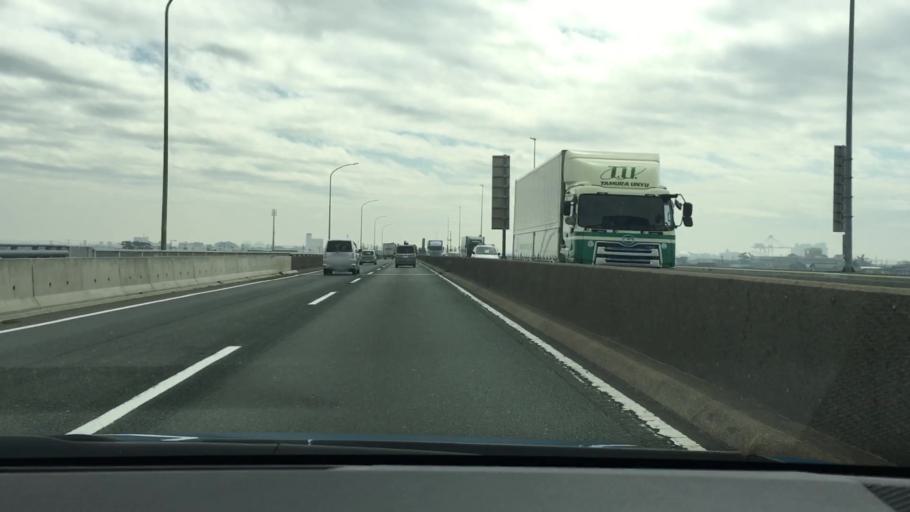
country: JP
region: Aichi
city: Kozakai-cho
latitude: 34.7774
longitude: 137.3326
